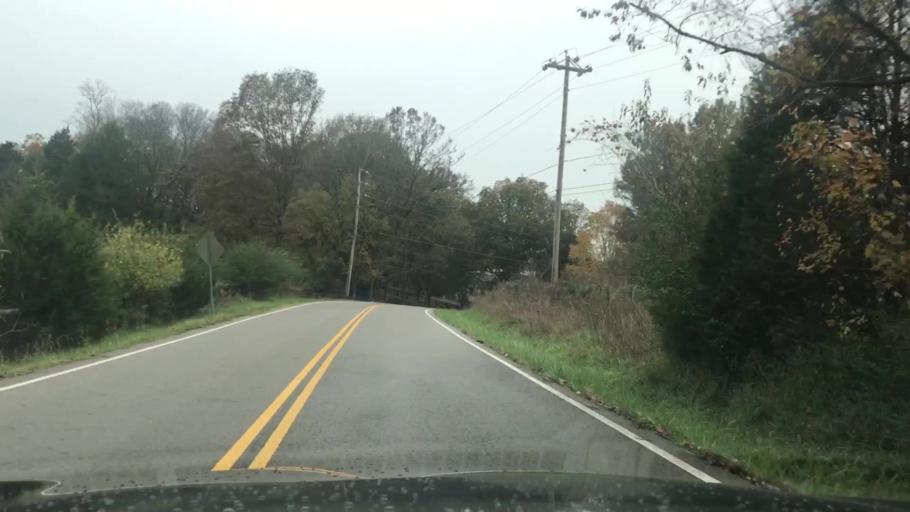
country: US
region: Tennessee
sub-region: Williamson County
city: Franklin
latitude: 35.8952
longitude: -86.8181
